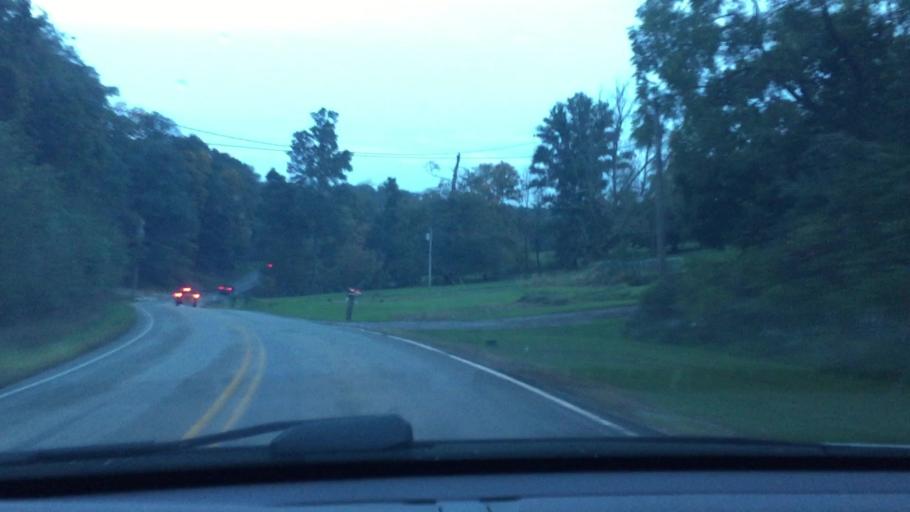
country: US
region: Pennsylvania
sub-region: Washington County
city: McGovern
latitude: 40.1949
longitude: -80.1955
